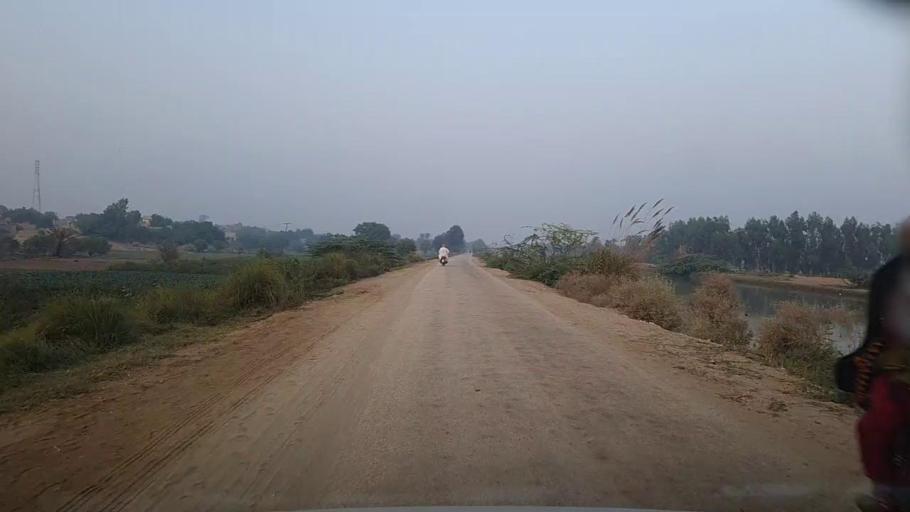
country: PK
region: Sindh
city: Bozdar
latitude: 27.0459
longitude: 68.5934
